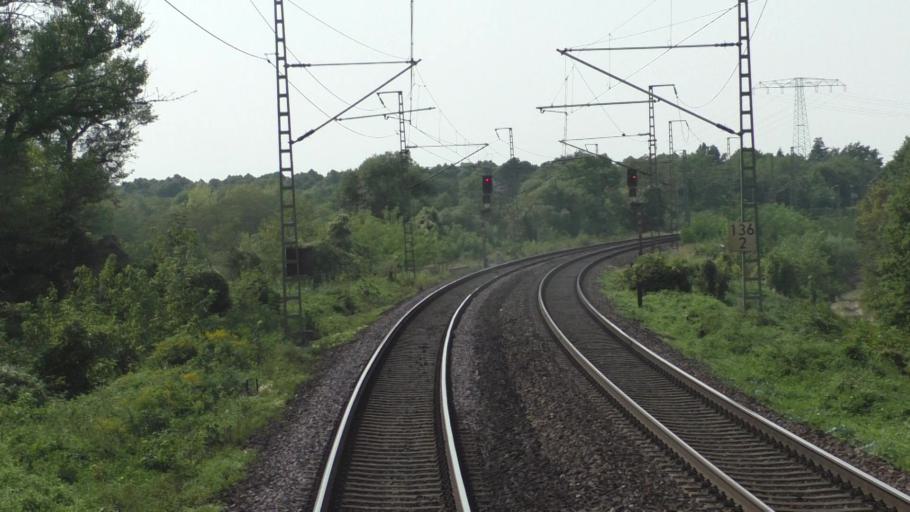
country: DE
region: Saxony-Anhalt
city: Biederitz
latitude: 52.1445
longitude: 11.6828
